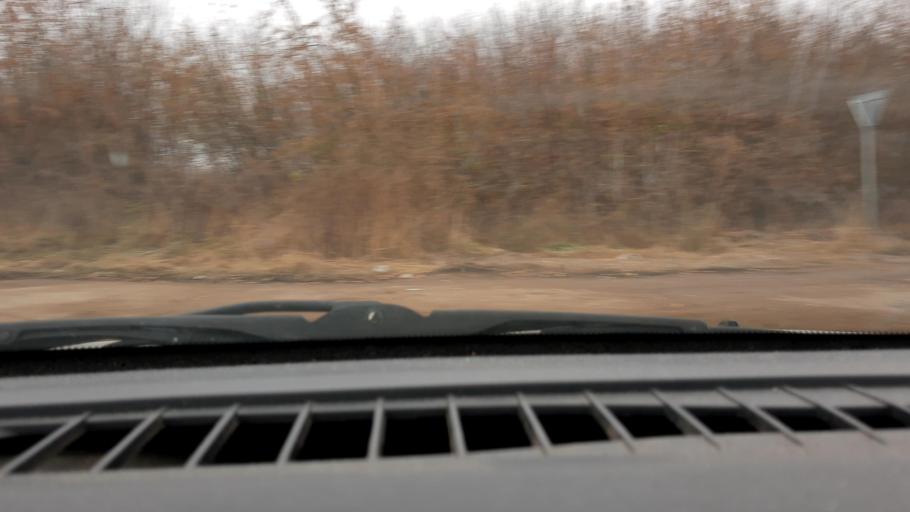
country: RU
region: Nizjnij Novgorod
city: Kstovo
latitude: 56.1970
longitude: 44.1529
